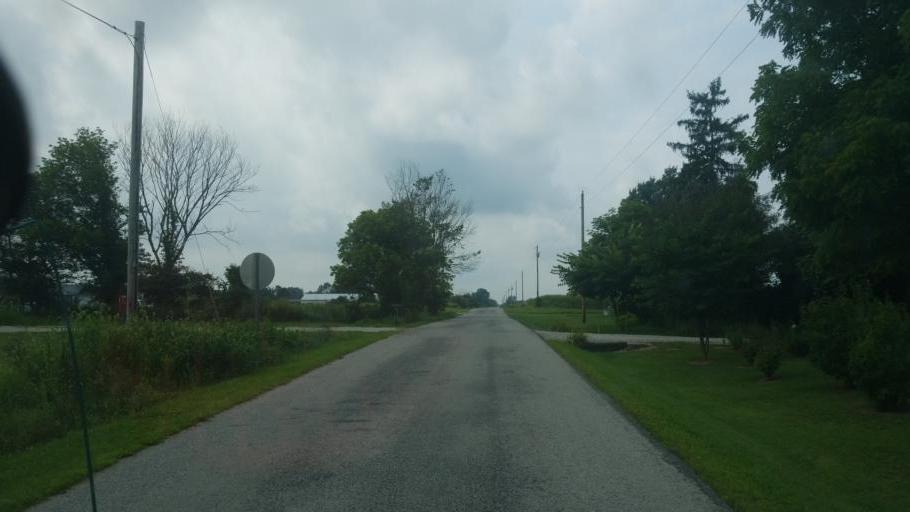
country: US
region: Ohio
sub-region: Huron County
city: Greenwich
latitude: 41.0615
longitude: -82.4616
